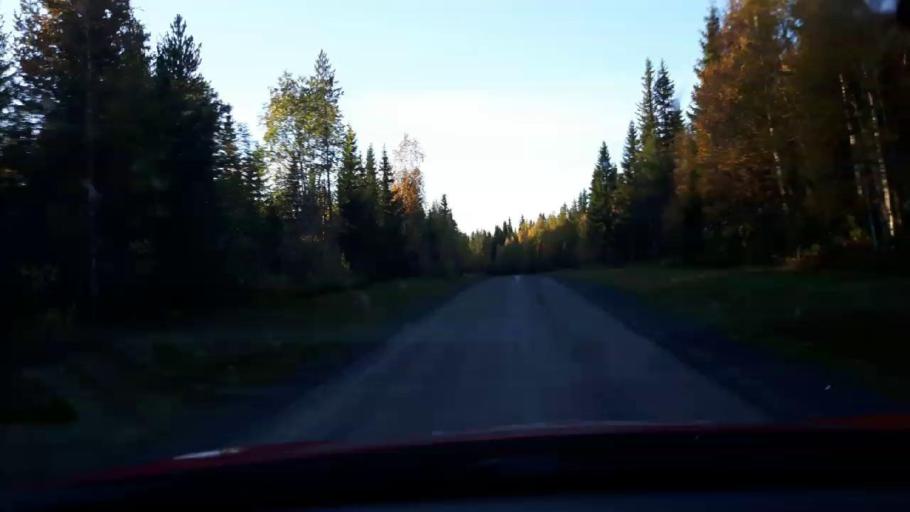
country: SE
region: Jaemtland
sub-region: Krokoms Kommun
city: Krokom
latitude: 63.4479
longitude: 14.5756
